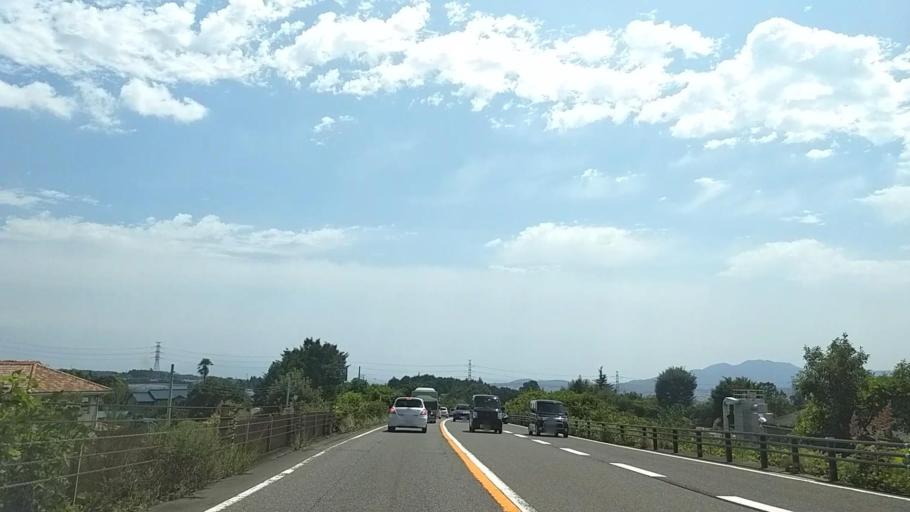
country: JP
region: Shizuoka
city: Fujinomiya
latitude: 35.2699
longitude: 138.6146
